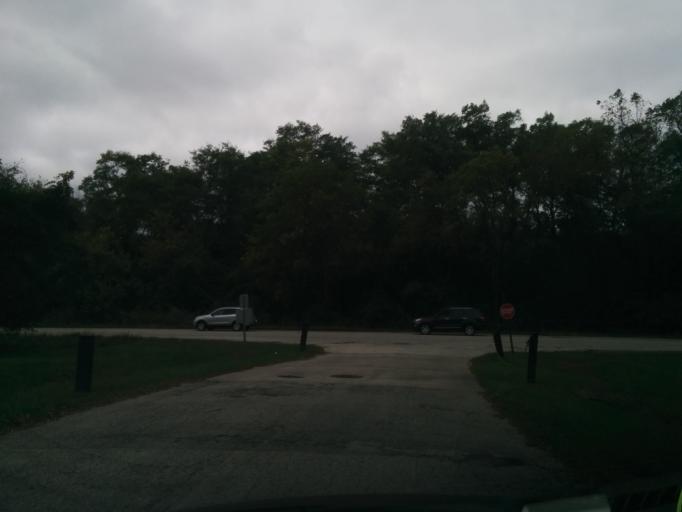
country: US
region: Illinois
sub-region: DuPage County
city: Burr Ridge
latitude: 41.7114
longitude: -87.9139
